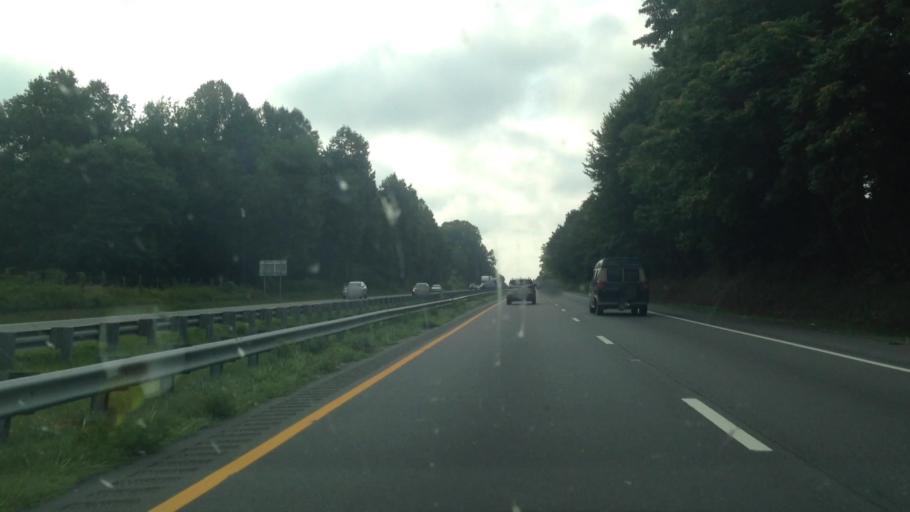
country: US
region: North Carolina
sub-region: Forsyth County
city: Kernersville
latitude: 36.1023
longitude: -80.0274
